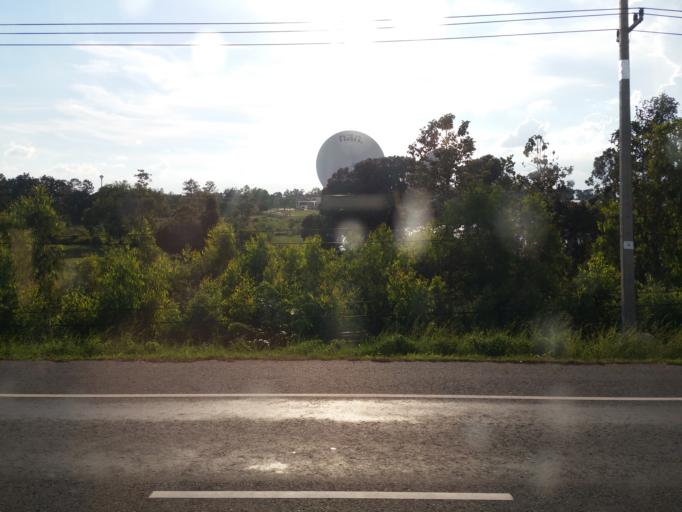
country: TH
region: Changwat Ubon Ratchathani
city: Sirindhorn
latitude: 15.1941
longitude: 105.3685
